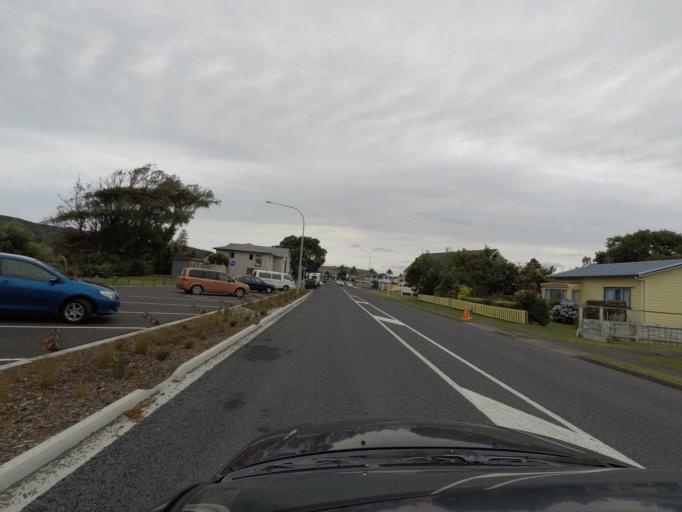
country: NZ
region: Waikato
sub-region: Waikato District
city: Raglan
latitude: -37.8027
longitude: 174.8685
